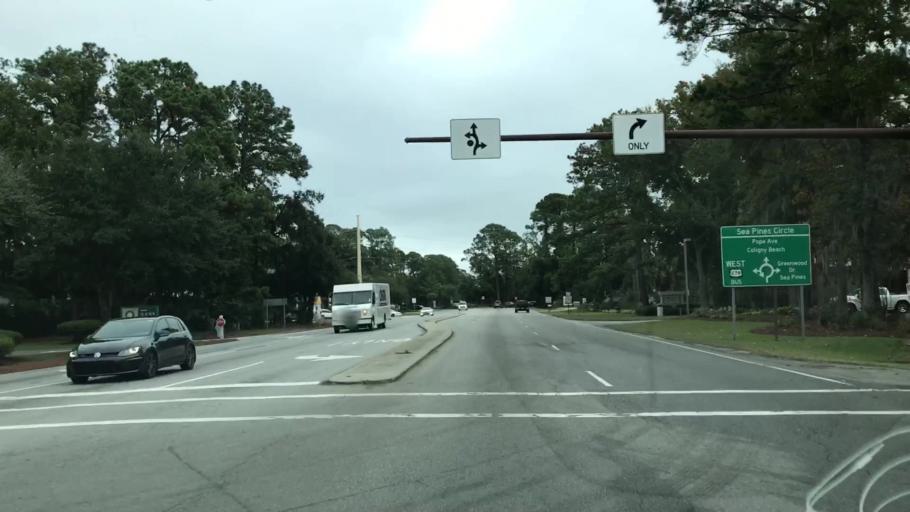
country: US
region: South Carolina
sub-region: Beaufort County
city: Hilton Head Island
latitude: 32.1578
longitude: -80.7646
